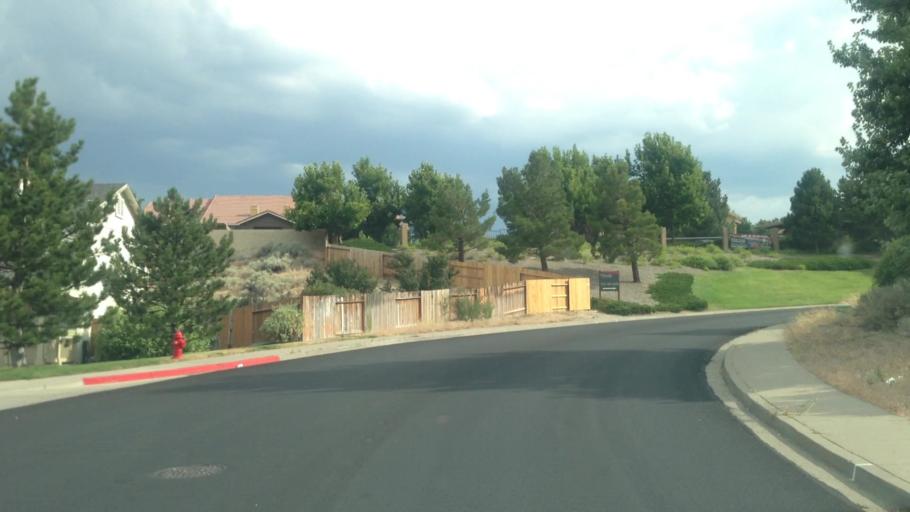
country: US
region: Nevada
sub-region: Washoe County
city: Reno
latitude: 39.5269
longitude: -119.8644
